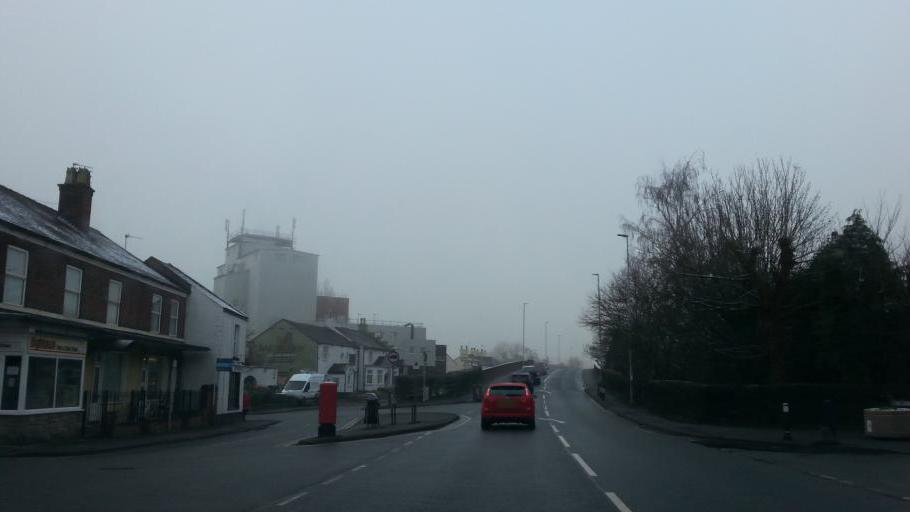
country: GB
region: England
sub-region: Cheshire East
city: Congleton
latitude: 53.1567
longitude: -2.1914
